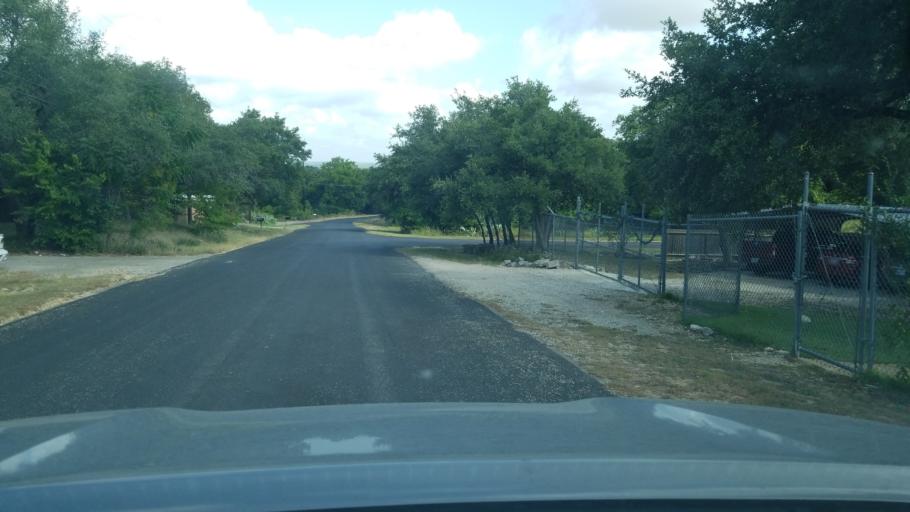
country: US
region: Texas
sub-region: Bexar County
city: Timberwood Park
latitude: 29.7081
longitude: -98.4817
